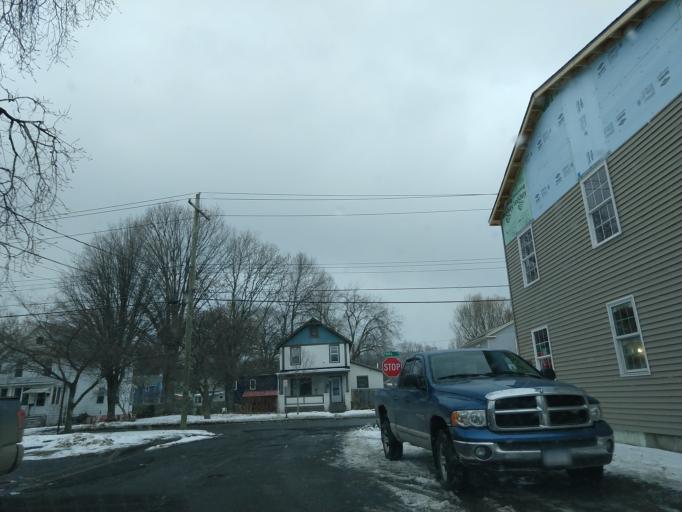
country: US
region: New York
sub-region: Tompkins County
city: Ithaca
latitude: 42.4458
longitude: -76.5052
